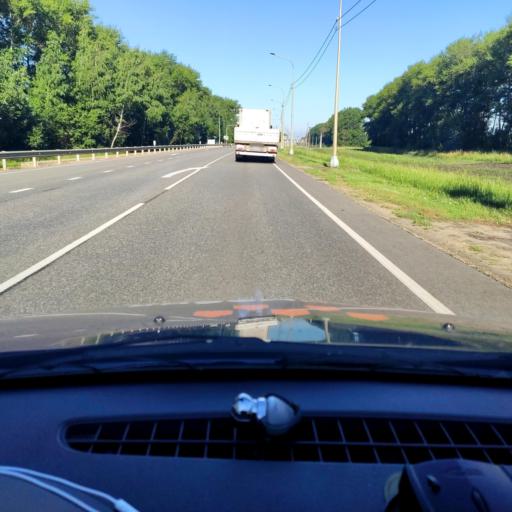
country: RU
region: Orjol
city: Zmiyevka
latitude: 52.6352
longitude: 36.6178
